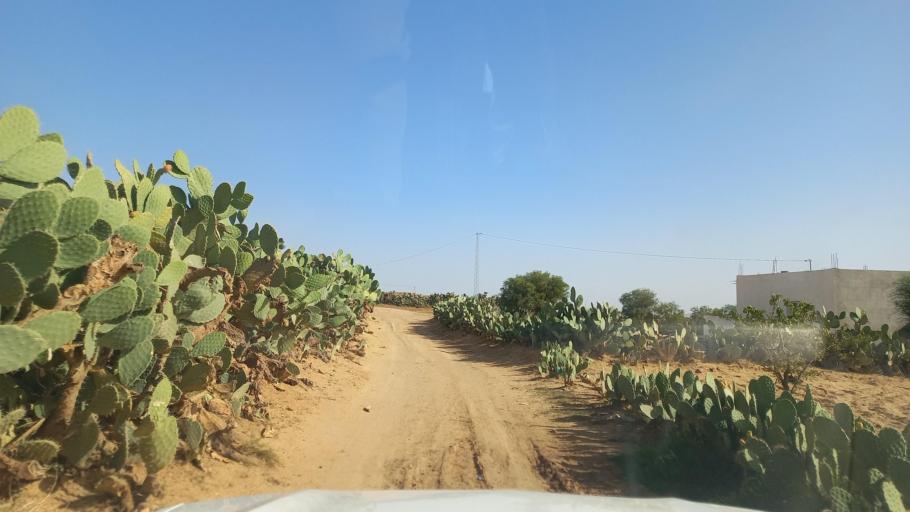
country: TN
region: Al Qasrayn
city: Sbiba
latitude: 35.3201
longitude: 9.0212
